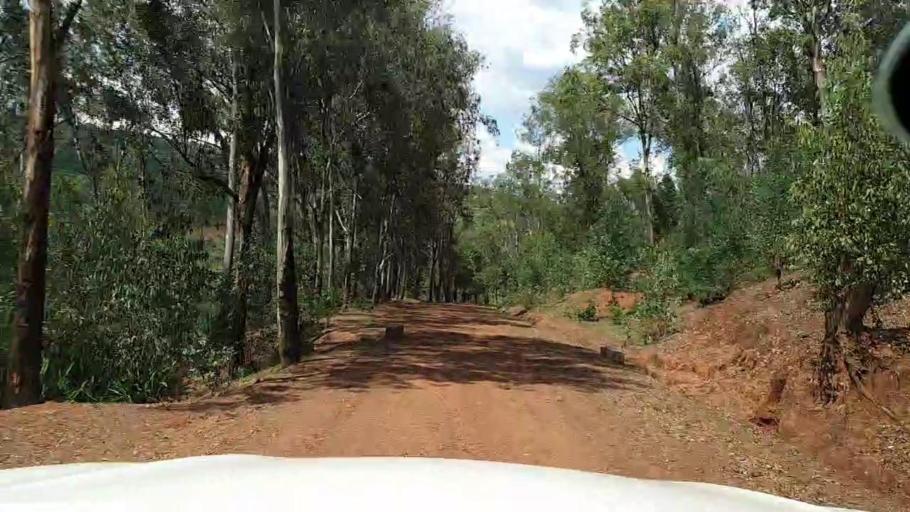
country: RW
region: Southern Province
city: Butare
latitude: -2.7528
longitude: 29.7014
